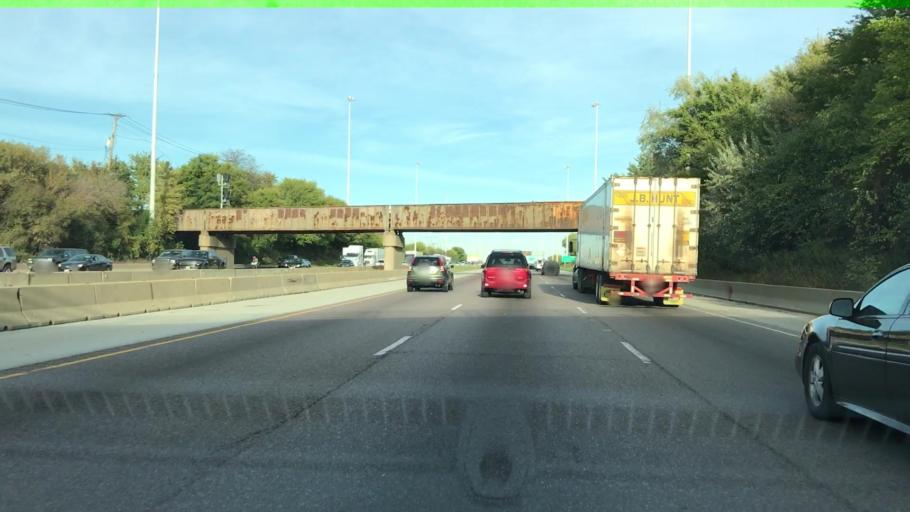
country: US
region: Illinois
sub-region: Cook County
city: Cicero
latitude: 41.8258
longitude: -87.7152
